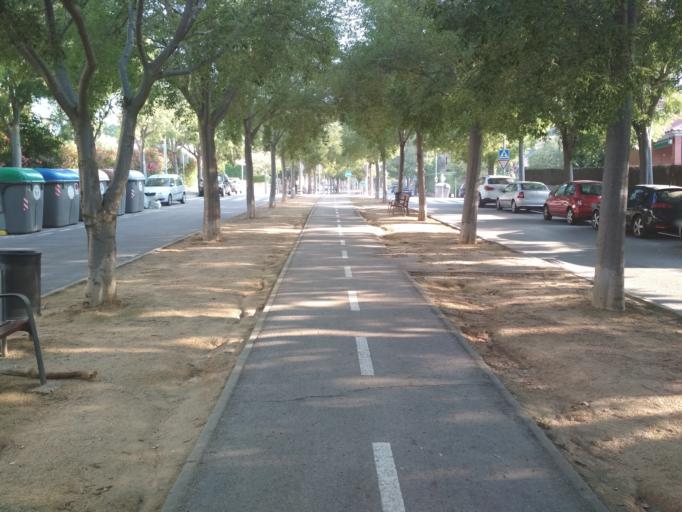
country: ES
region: Catalonia
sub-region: Provincia de Barcelona
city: Sant Cugat del Valles
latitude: 41.4698
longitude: 2.0722
